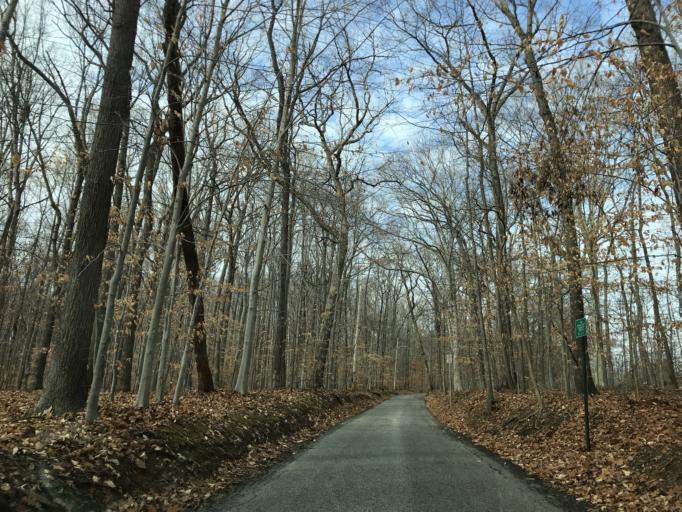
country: US
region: Maryland
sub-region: Baltimore County
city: Kingsville
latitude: 39.4398
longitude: -76.3909
